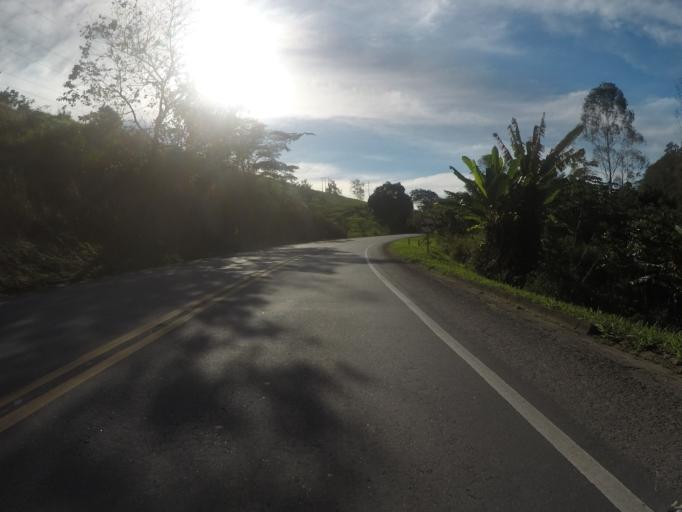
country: BR
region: Espirito Santo
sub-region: Fundao
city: Fundao
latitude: -19.8972
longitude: -40.4111
